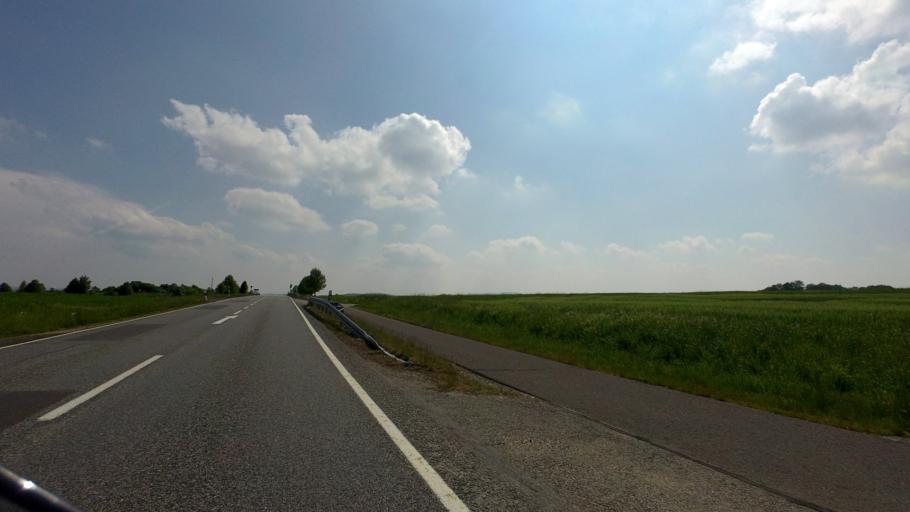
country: DE
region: Saxony
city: Weissenberg
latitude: 51.2095
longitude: 14.6640
